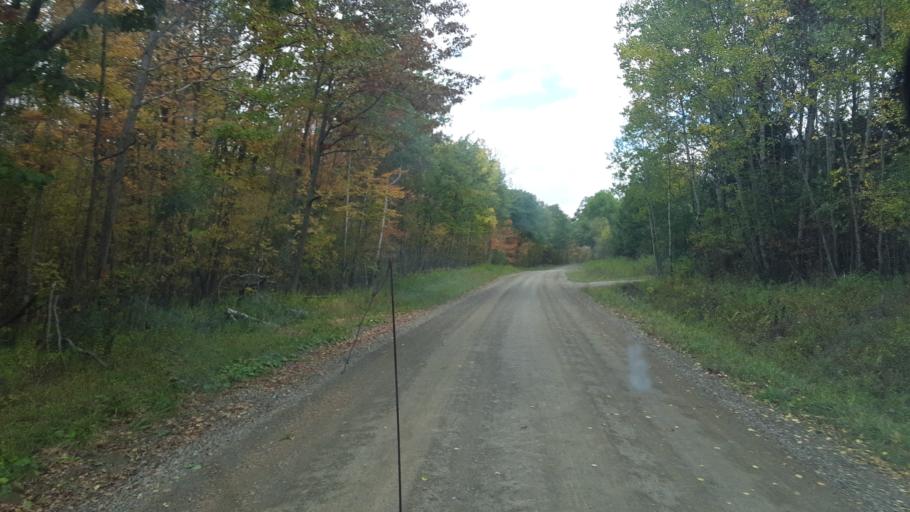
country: US
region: New York
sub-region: Allegany County
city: Alfred
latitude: 42.3810
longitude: -77.8569
